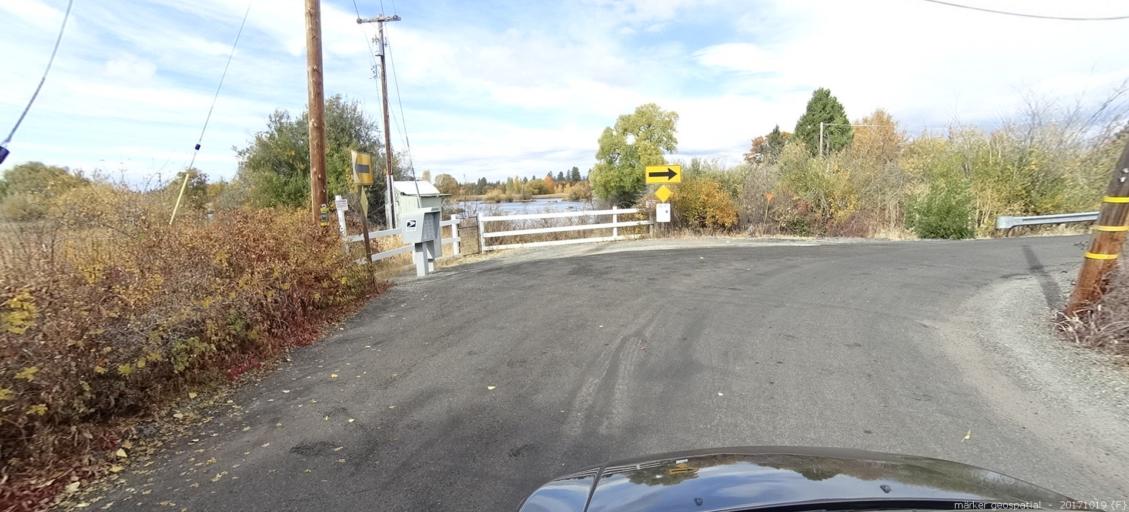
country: US
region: California
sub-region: Shasta County
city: Burney
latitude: 41.1092
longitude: -121.4922
